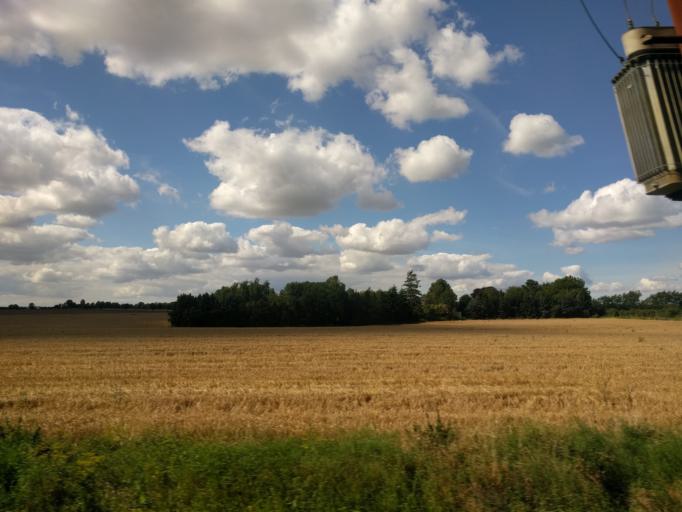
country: DK
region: Zealand
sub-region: Roskilde Kommune
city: Svogerslev
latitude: 55.6102
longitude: 12.0473
